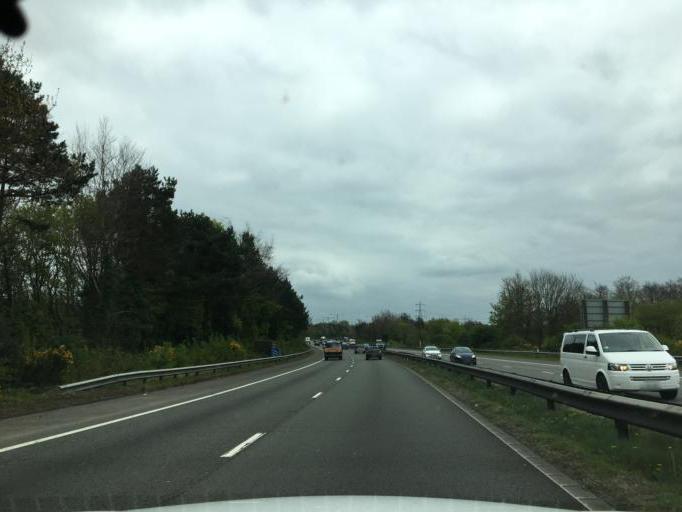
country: GB
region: Wales
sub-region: City and County of Swansea
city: Clydach
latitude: 51.6678
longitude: -3.8874
